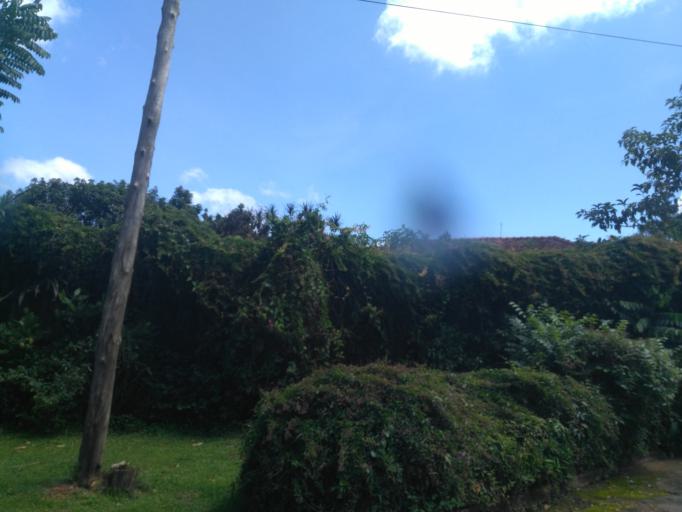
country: UG
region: Central Region
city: Kampala Central Division
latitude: 0.3265
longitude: 32.5785
